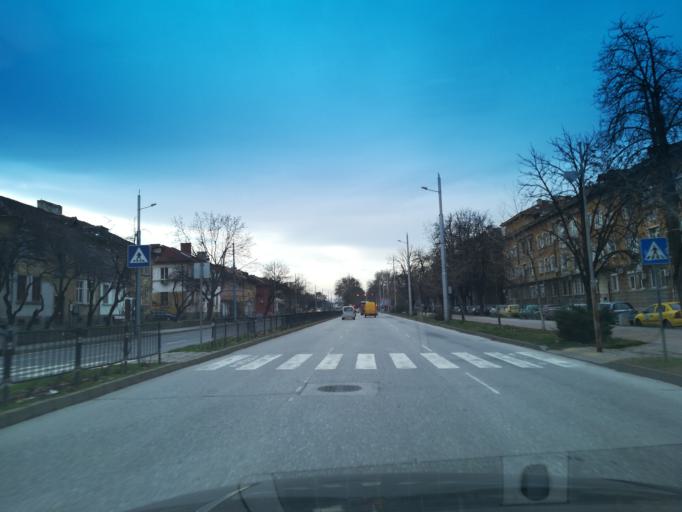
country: BG
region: Plovdiv
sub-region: Obshtina Plovdiv
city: Plovdiv
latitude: 42.1344
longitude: 24.7380
